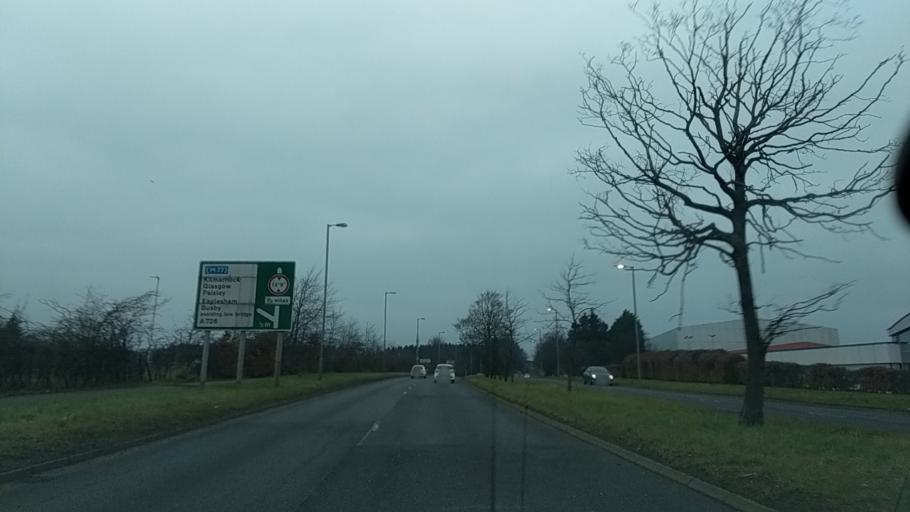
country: GB
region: Scotland
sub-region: Glasgow City
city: Carmunnock
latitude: 55.7659
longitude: -4.2139
